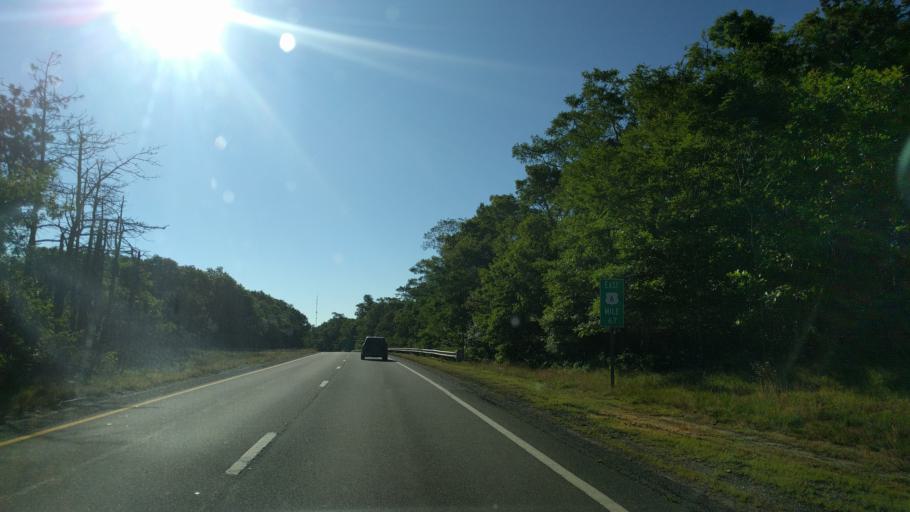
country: US
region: Massachusetts
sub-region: Barnstable County
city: West Barnstable
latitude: 41.6844
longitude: -70.3594
